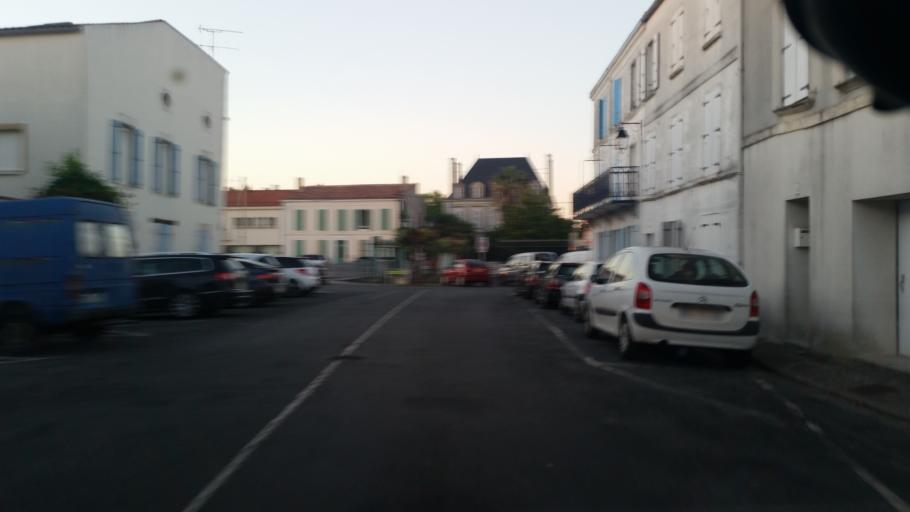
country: FR
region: Poitou-Charentes
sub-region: Departement de la Charente-Maritime
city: Marans
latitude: 46.3114
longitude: -0.9951
